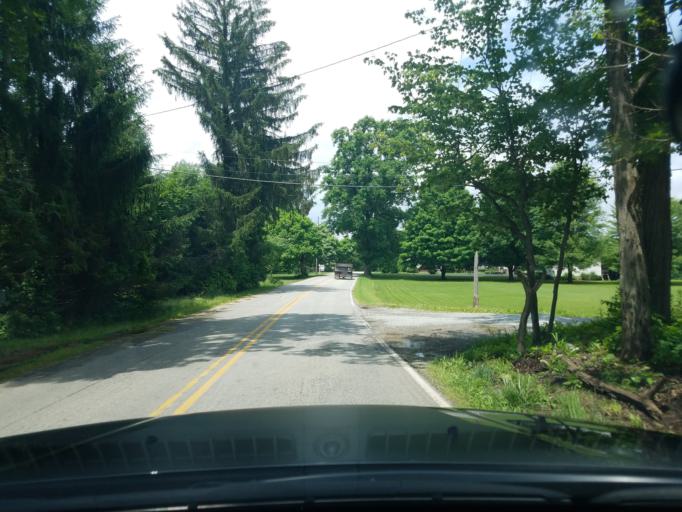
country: US
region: Pennsylvania
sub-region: Fayette County
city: Bear Rocks
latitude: 40.1525
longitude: -79.3387
